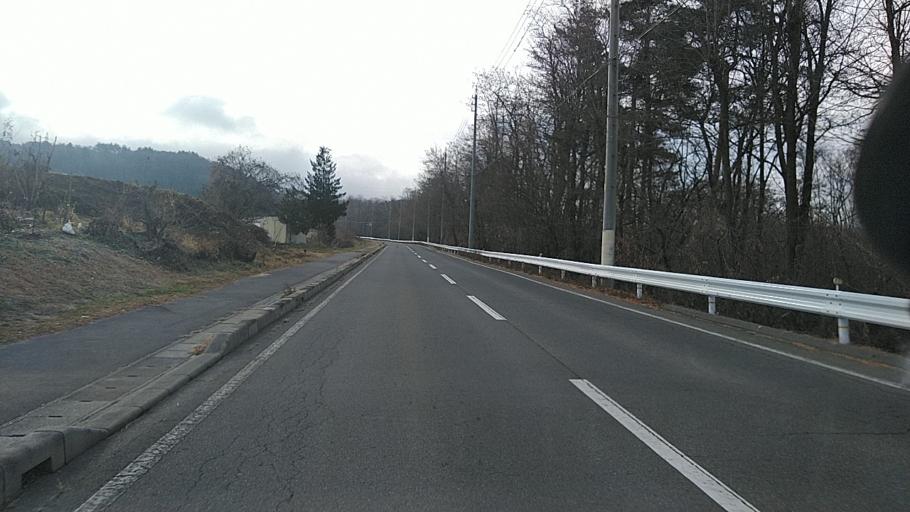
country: JP
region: Nagano
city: Matsumoto
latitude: 36.1759
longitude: 137.9971
